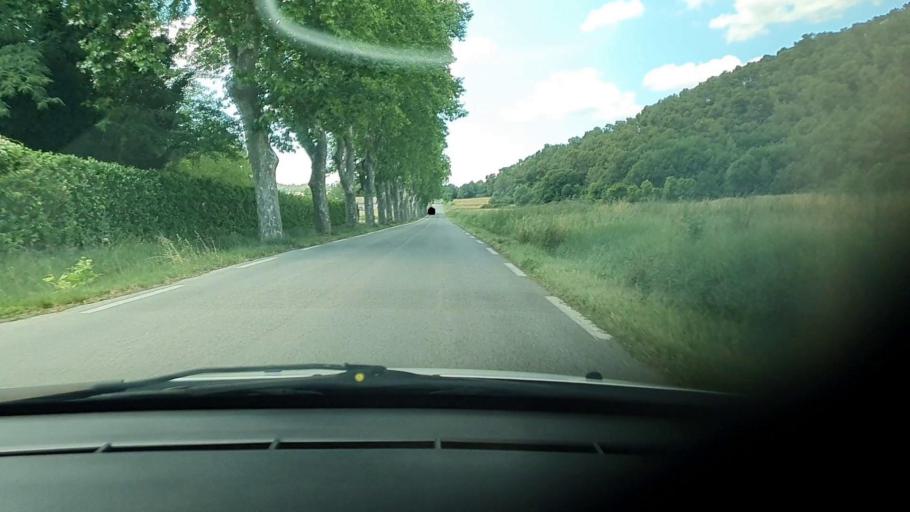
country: FR
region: Languedoc-Roussillon
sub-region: Departement du Gard
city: Montaren-et-Saint-Mediers
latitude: 44.0319
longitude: 4.3704
